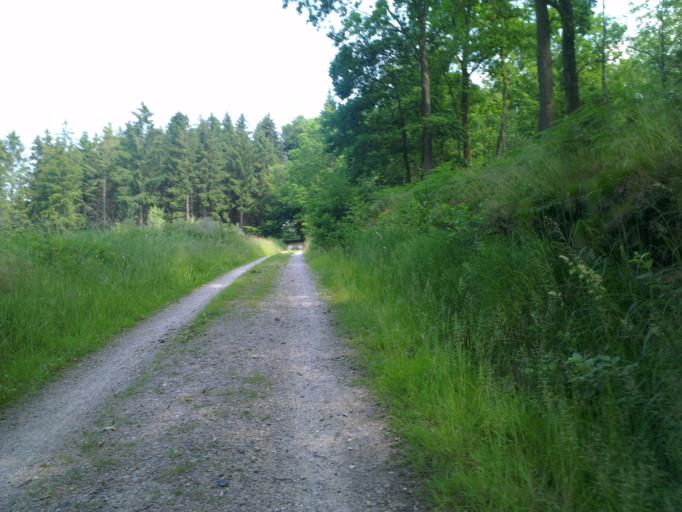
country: DK
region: Capital Region
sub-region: Allerod Kommune
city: Lillerod
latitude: 55.9070
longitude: 12.3573
